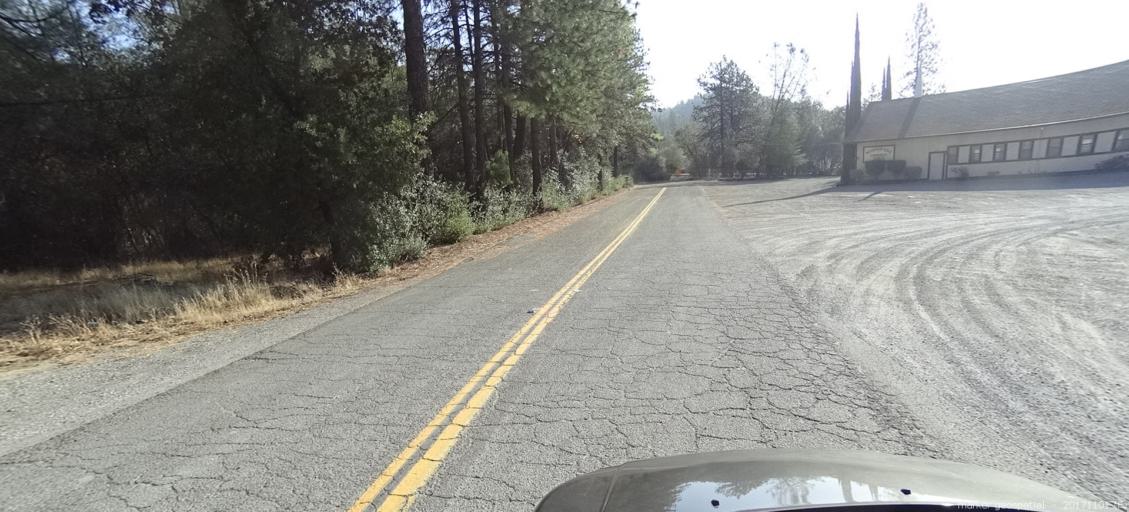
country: US
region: California
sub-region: Shasta County
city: Shasta Lake
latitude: 40.7381
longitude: -122.3173
